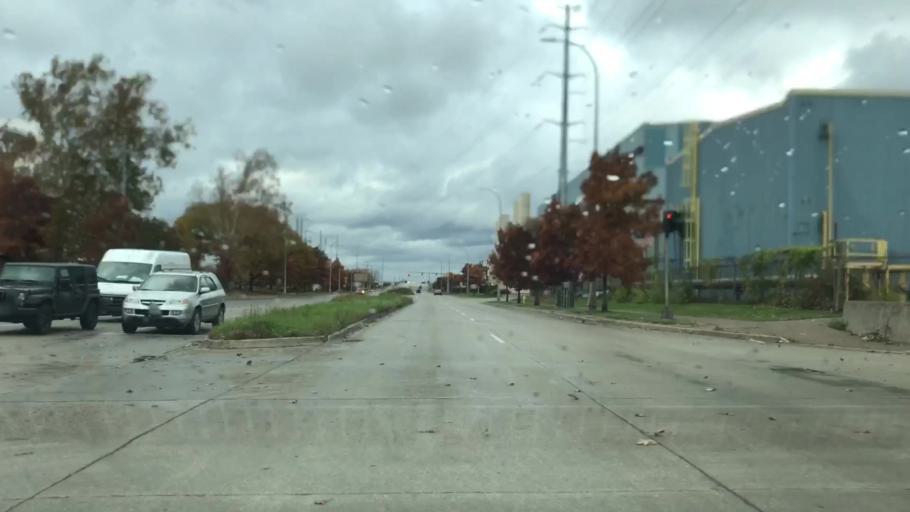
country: US
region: Michigan
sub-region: Wayne County
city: Dearborn
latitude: 42.3098
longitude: -83.1572
